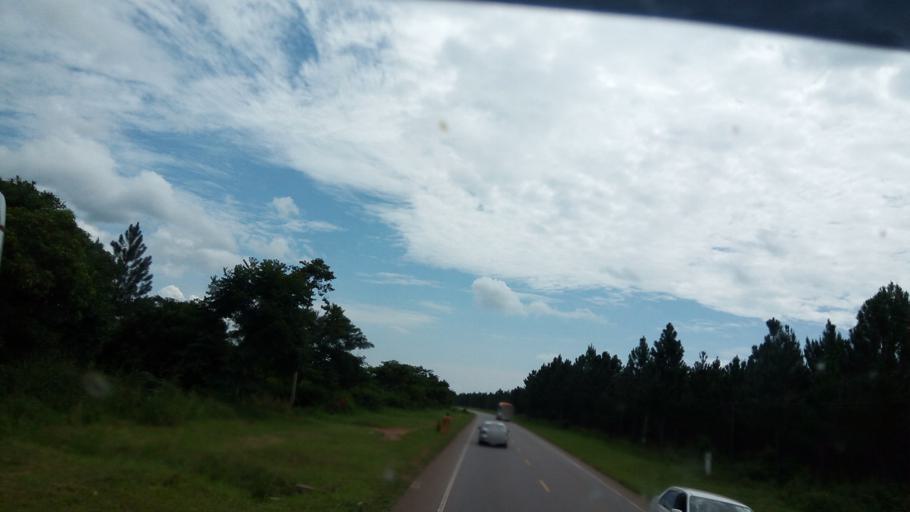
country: UG
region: Central Region
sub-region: Nakasongola District
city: Nakasongola
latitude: 1.2177
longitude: 32.4649
